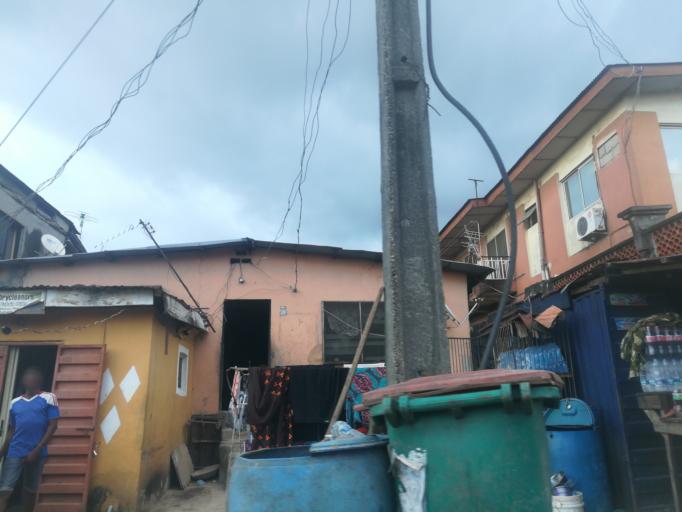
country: NG
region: Lagos
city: Somolu
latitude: 6.5570
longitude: 3.3852
